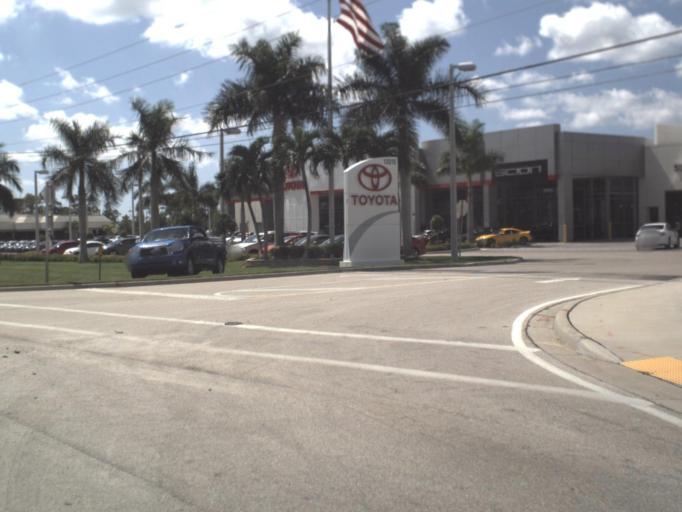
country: US
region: Florida
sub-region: Collier County
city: Naples Park
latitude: 26.2926
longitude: -81.8021
